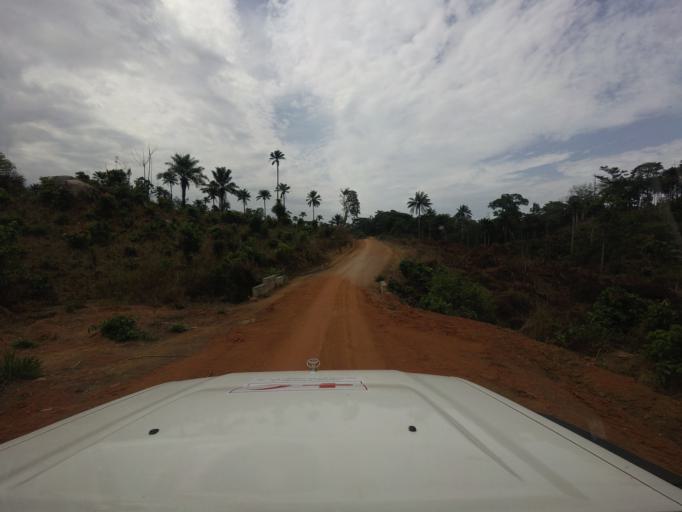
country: SL
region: Eastern Province
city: Buedu
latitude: 8.2479
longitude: -10.2235
